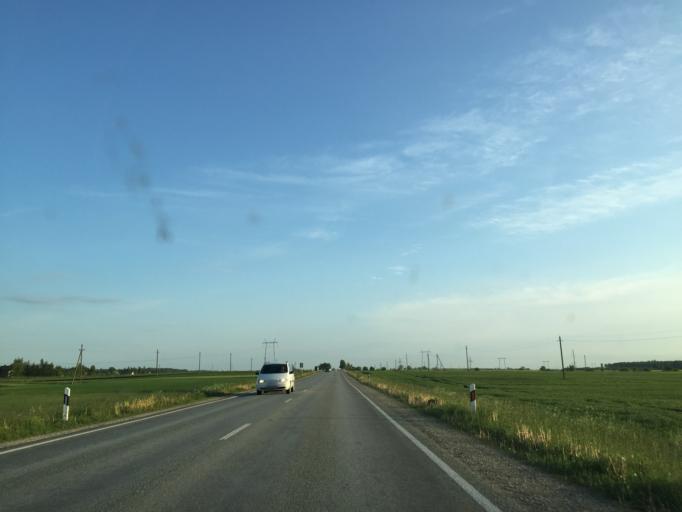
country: LT
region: Siauliu apskritis
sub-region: Joniskis
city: Joniskis
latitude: 56.1135
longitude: 23.4920
